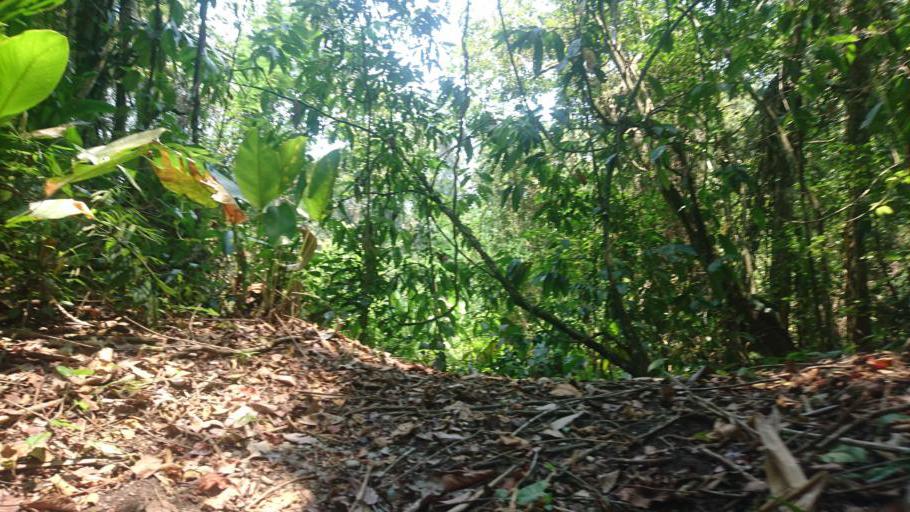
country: MX
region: Chiapas
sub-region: Marques de Comillas
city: Zamora Pico de Oro
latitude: 16.2483
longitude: -90.8348
